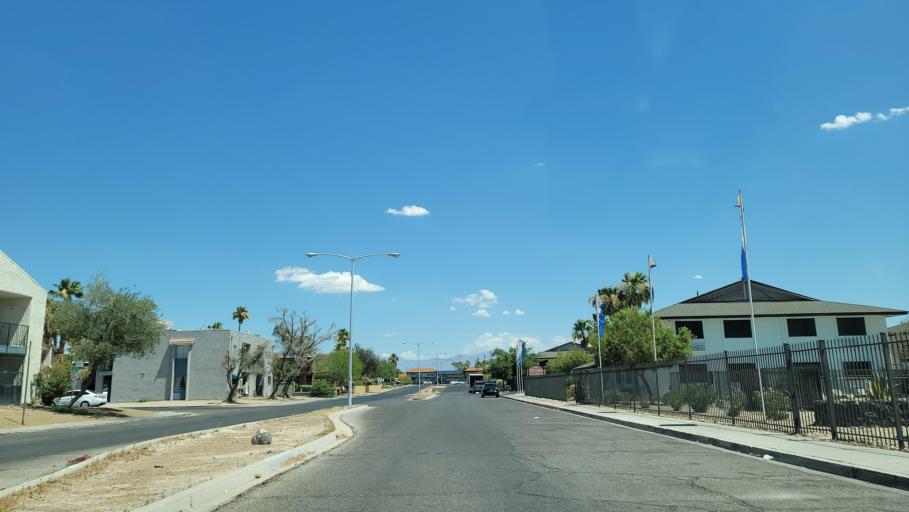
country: US
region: Nevada
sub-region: Clark County
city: Spring Valley
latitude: 36.1236
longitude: -115.2030
